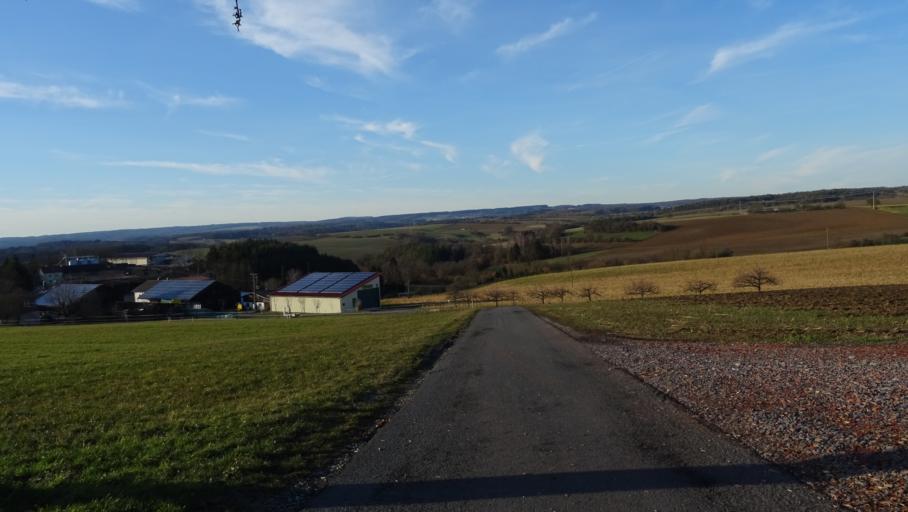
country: DE
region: Baden-Wuerttemberg
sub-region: Karlsruhe Region
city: Billigheim
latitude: 49.4103
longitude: 9.2624
